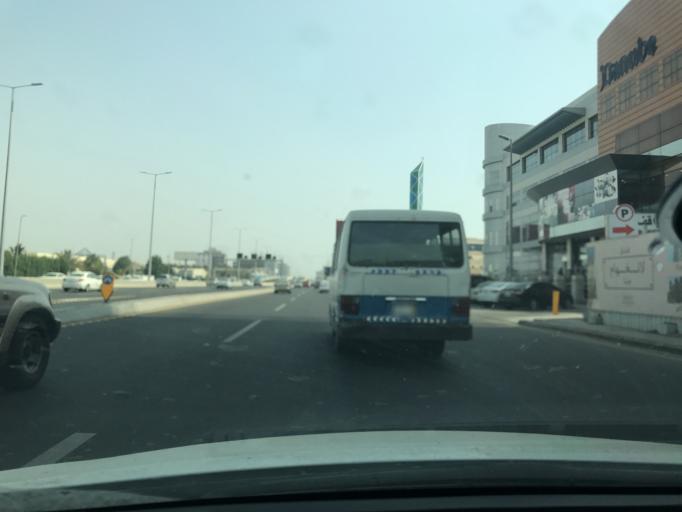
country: SA
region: Makkah
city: Jeddah
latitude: 21.6200
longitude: 39.1541
